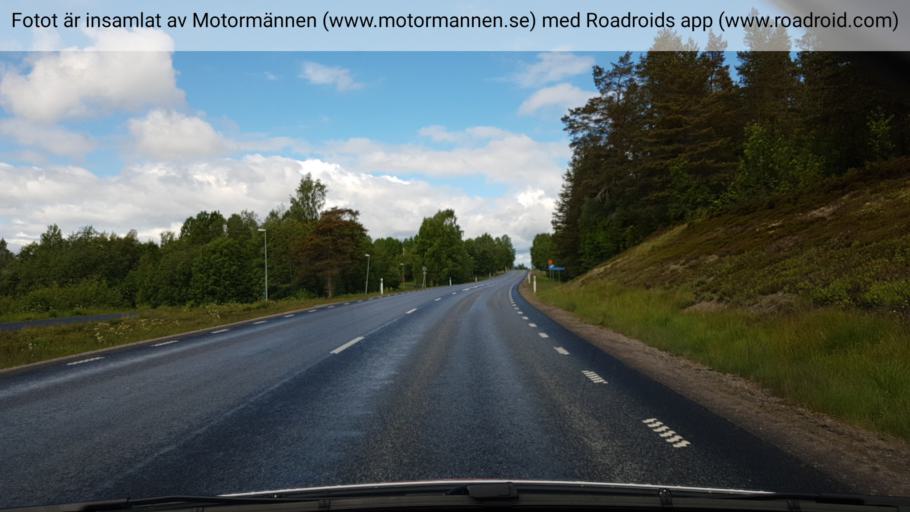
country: SE
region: Vaesterbotten
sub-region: Umea Kommun
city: Roback
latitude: 63.8561
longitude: 20.0960
